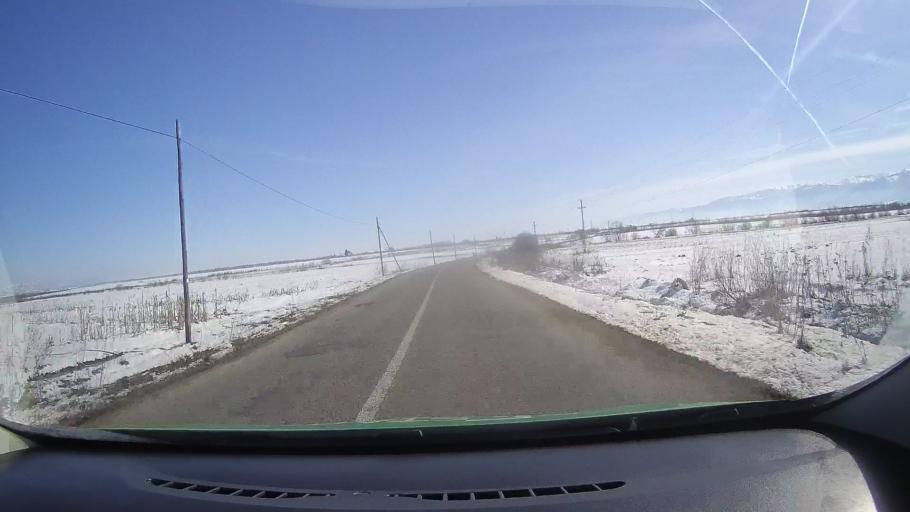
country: RO
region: Brasov
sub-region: Comuna Sambata de Sus
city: Sambata de Sus
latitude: 45.7628
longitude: 24.8002
